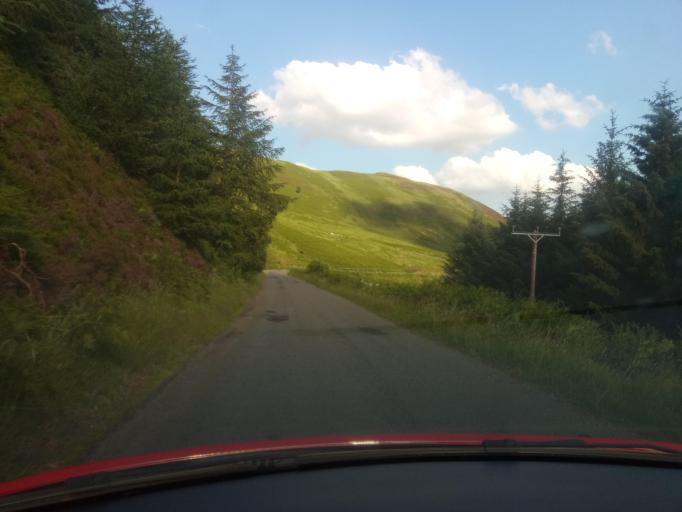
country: GB
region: Scotland
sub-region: The Scottish Borders
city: Innerleithen
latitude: 55.4658
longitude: -3.1305
